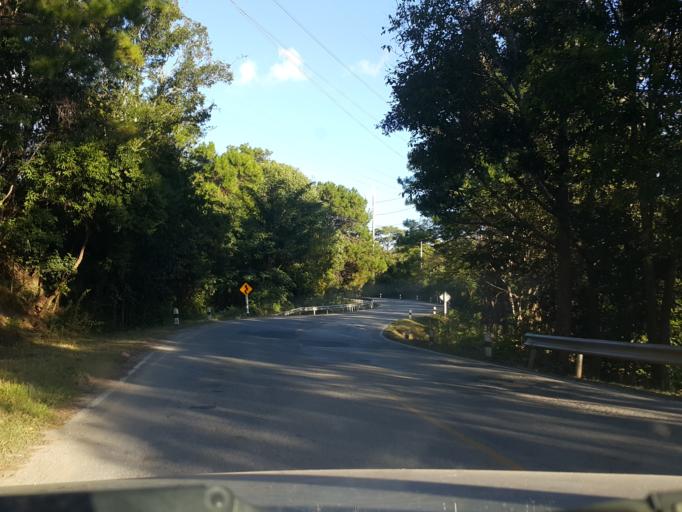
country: TH
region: Mae Hong Son
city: Mae Hi
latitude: 19.2725
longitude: 98.5544
